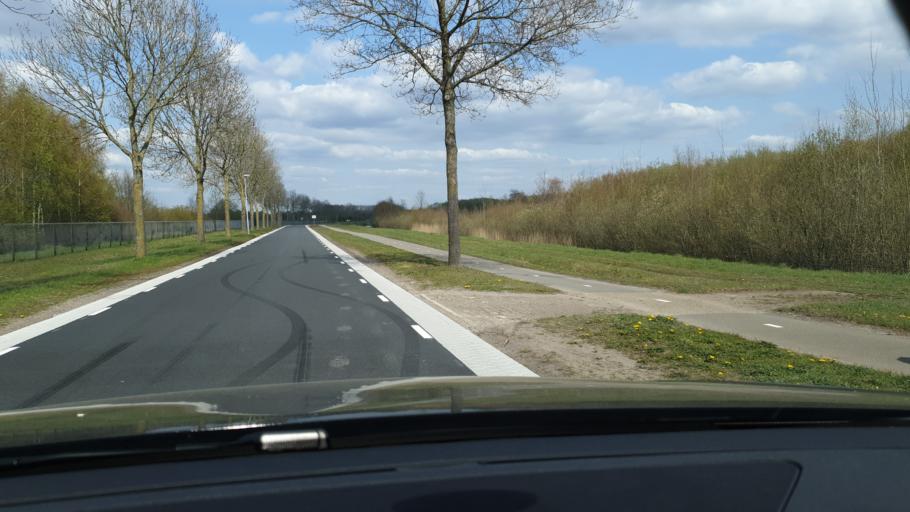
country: NL
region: North Brabant
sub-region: Gemeente Eindhoven
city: Meerhoven
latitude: 51.4638
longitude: 5.3793
